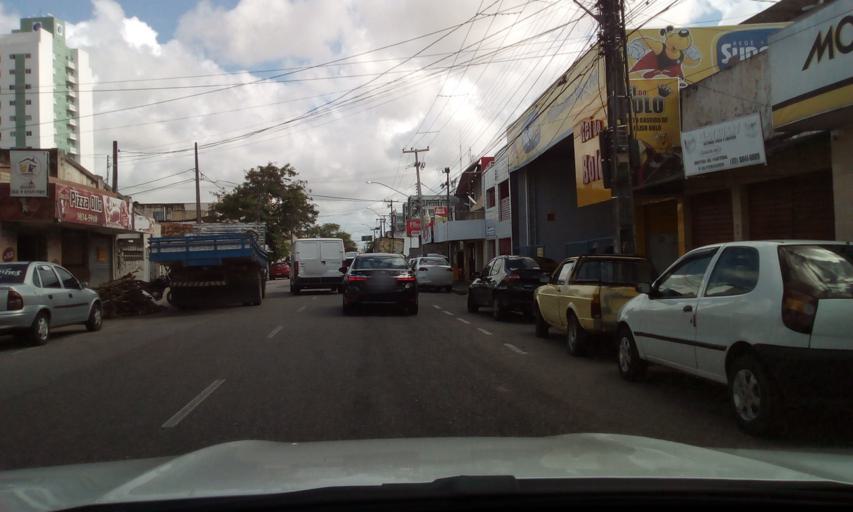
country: BR
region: Paraiba
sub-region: Joao Pessoa
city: Joao Pessoa
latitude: -7.1305
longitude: -34.8805
